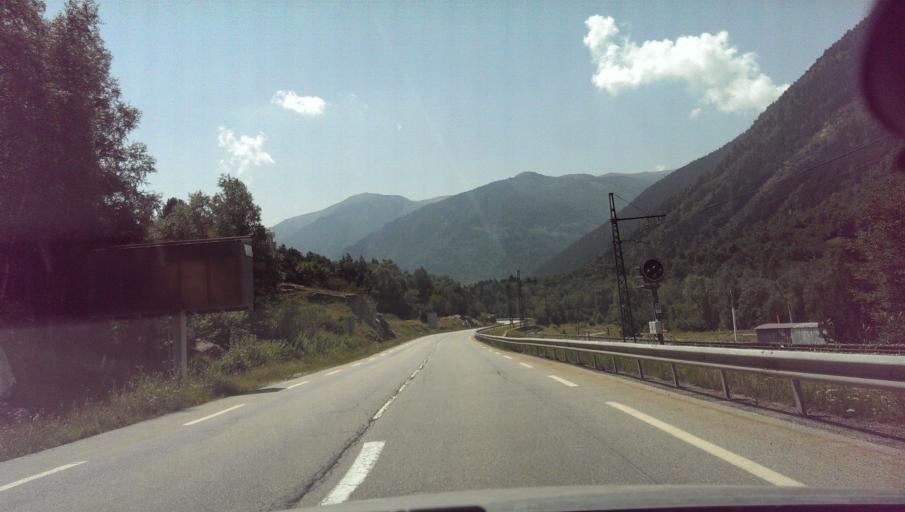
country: AD
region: Encamp
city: Pas de la Casa
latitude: 42.5345
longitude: 1.8225
